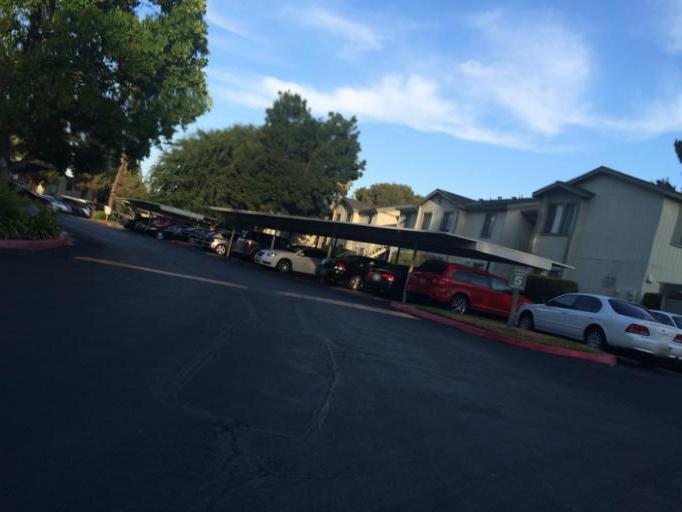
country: US
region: California
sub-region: Fresno County
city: Tarpey Village
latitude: 36.7918
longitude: -119.7188
